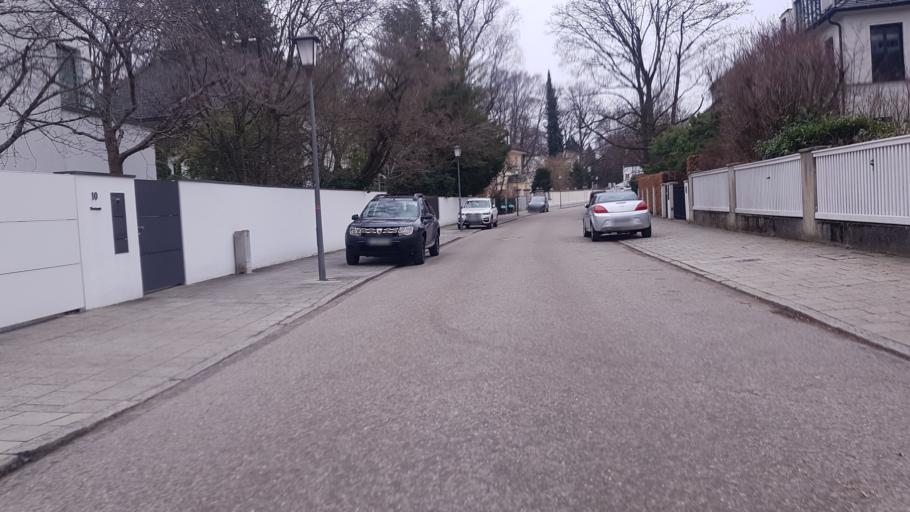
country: DE
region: Bavaria
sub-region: Upper Bavaria
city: Bogenhausen
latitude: 48.1484
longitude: 11.6102
